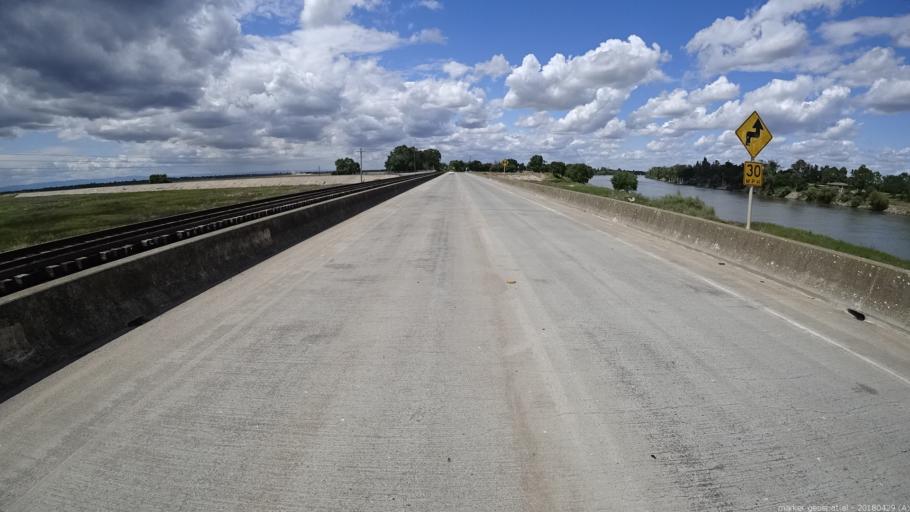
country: US
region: California
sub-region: Yolo County
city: West Sacramento
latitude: 38.6057
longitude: -121.5584
